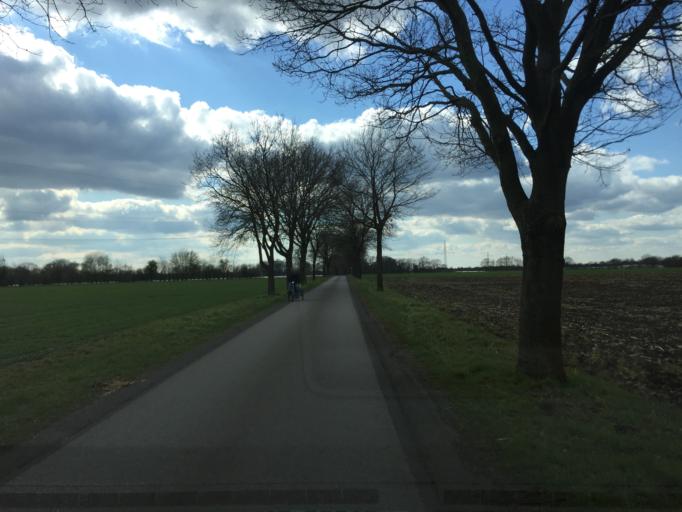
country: DE
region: Lower Saxony
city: Hassel
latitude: 52.6727
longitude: 8.8410
